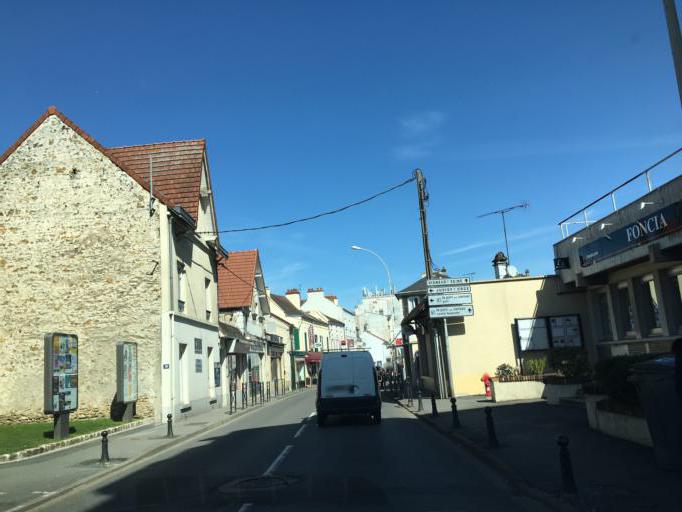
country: FR
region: Ile-de-France
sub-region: Departement de l'Essonne
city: Draveil
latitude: 48.6851
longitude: 2.4086
